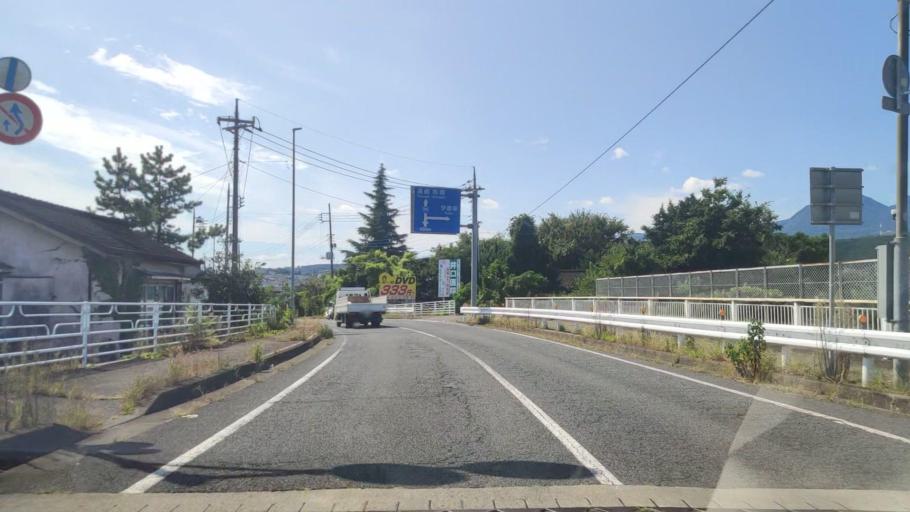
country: JP
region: Gunma
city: Shibukawa
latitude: 36.5136
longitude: 139.0057
